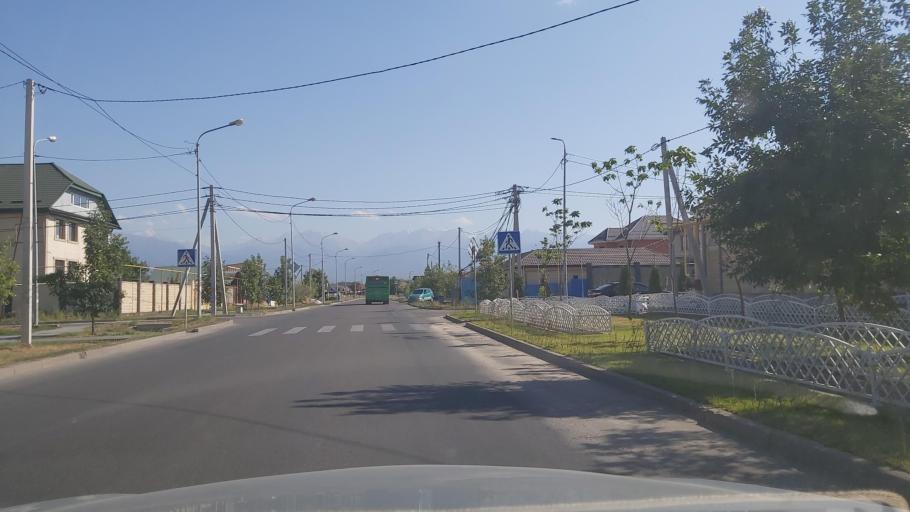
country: KZ
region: Almaty Oblysy
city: Burunday
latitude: 43.3161
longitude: 76.8421
